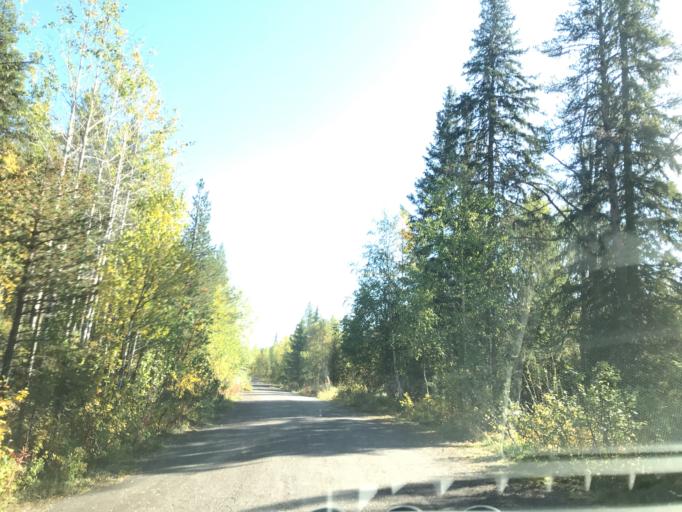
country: SE
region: Norrbotten
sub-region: Gallivare Kommun
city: Malmberget
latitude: 67.6462
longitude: 21.1052
